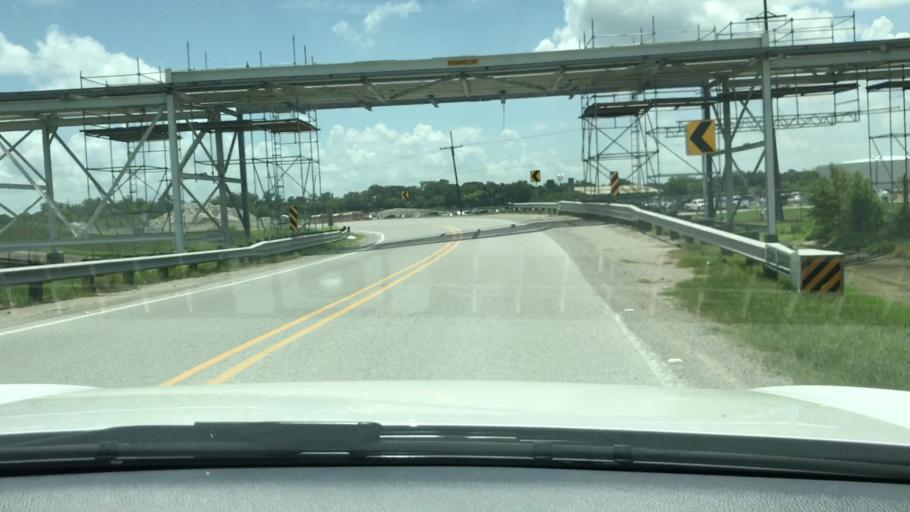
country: US
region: Louisiana
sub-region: Iberville Parish
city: Plaquemine
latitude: 30.2731
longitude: -91.1713
